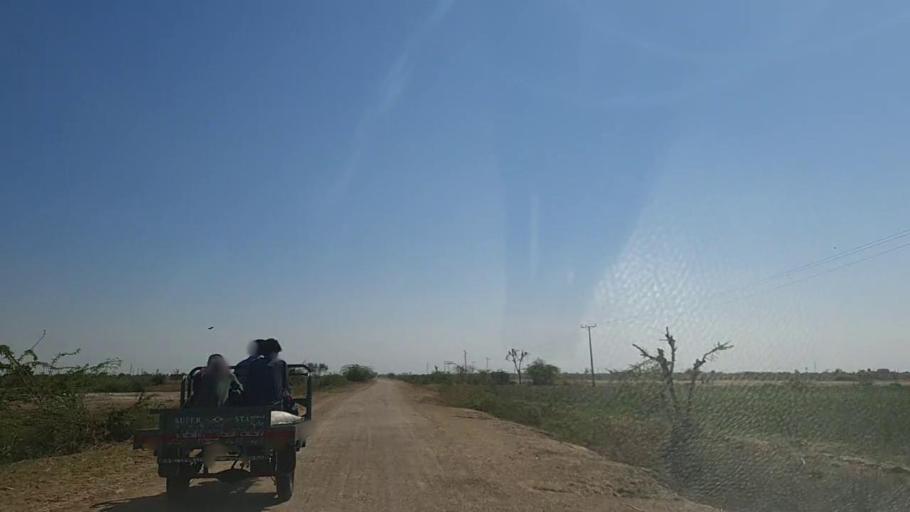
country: PK
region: Sindh
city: Samaro
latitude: 25.3084
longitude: 69.4773
